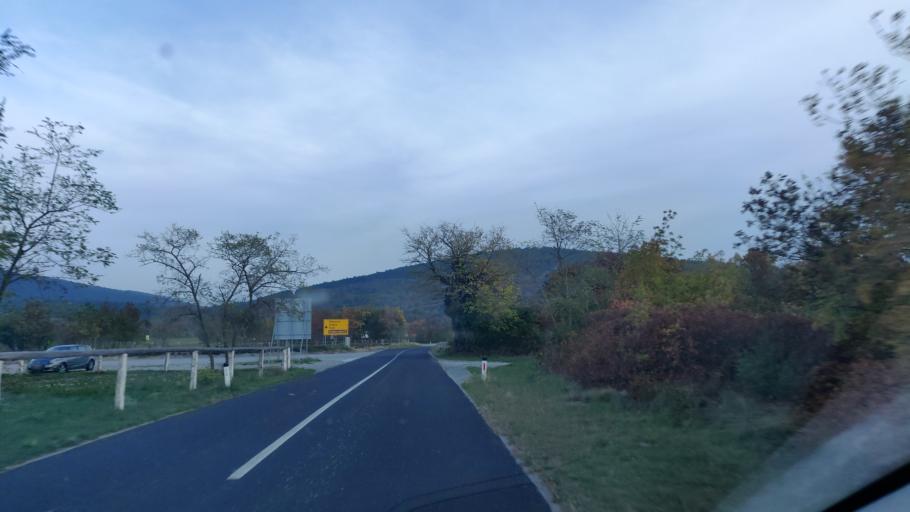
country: SI
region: Sezana
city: Sezana
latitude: 45.7406
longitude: 13.9315
